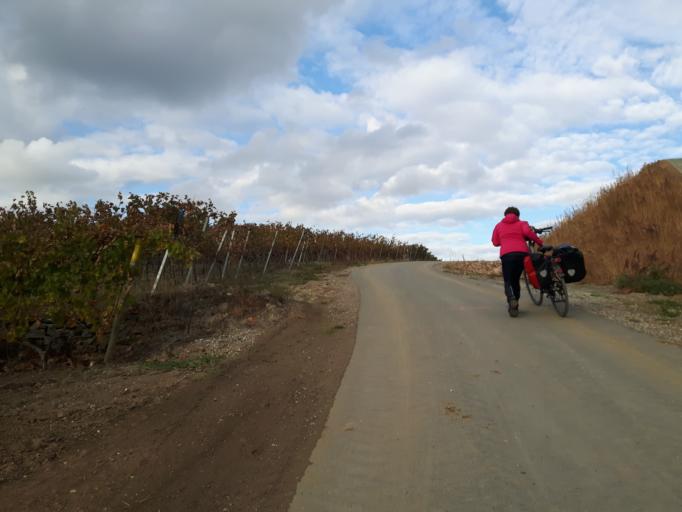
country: DE
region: Rheinland-Pfalz
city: Kirchheim an der Weinstrasse
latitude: 49.5405
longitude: 8.1718
